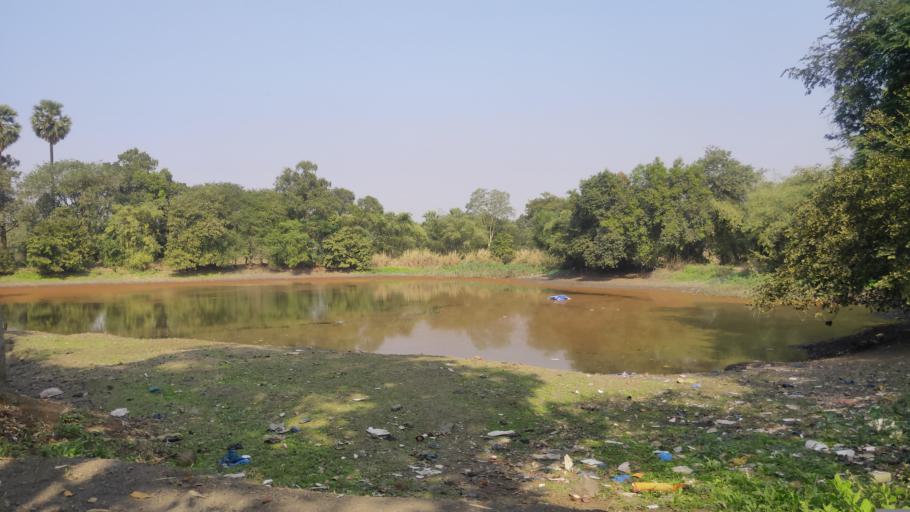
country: IN
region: Maharashtra
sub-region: Thane
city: Bhiwandi
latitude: 19.3374
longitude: 73.0946
